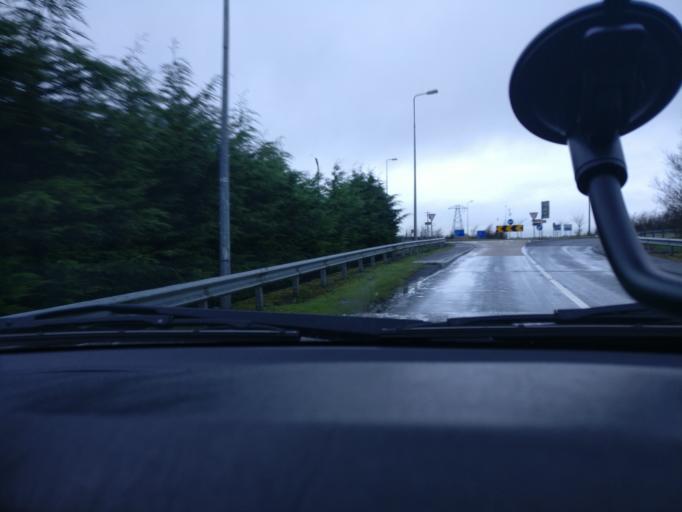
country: IE
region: Connaught
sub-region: County Galway
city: Loughrea
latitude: 53.2640
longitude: -8.6075
